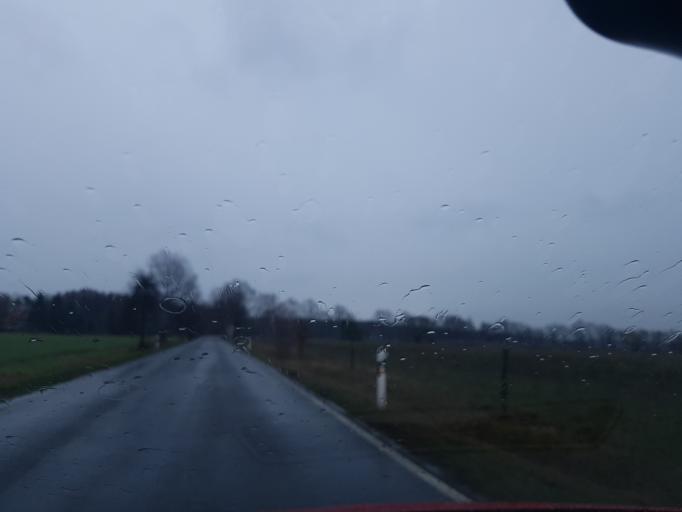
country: DE
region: Brandenburg
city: Schilda
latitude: 51.6265
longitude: 13.3152
